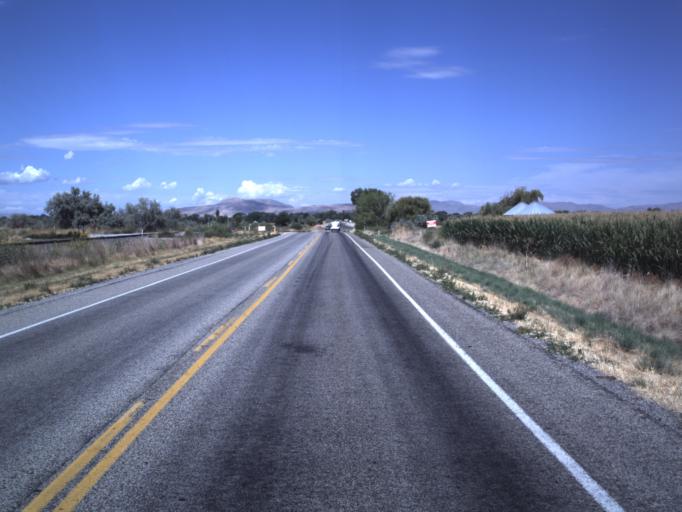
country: US
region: Utah
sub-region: Box Elder County
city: Brigham City
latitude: 41.5417
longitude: -112.0870
